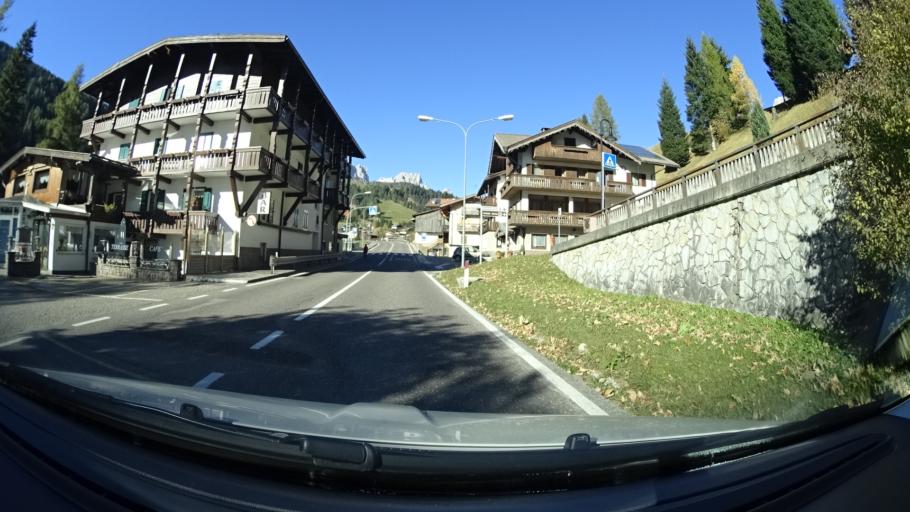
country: IT
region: Trentino-Alto Adige
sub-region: Provincia di Trento
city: Soraga
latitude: 46.3918
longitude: 11.6668
